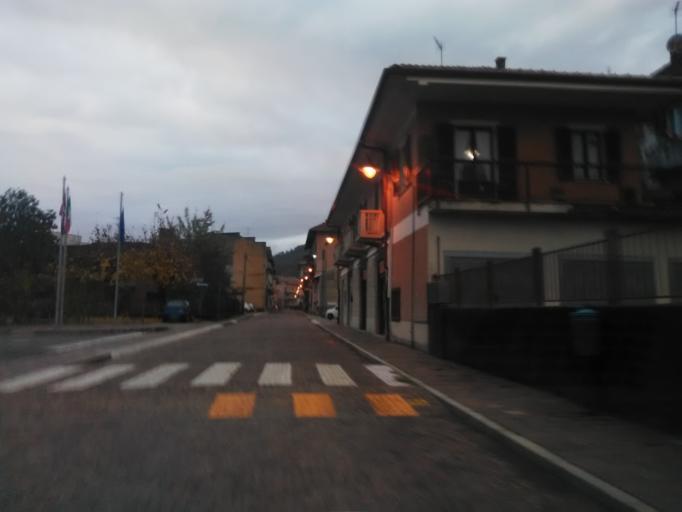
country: IT
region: Piedmont
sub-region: Provincia di Novara
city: Grignasco
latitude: 45.6828
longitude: 8.3407
